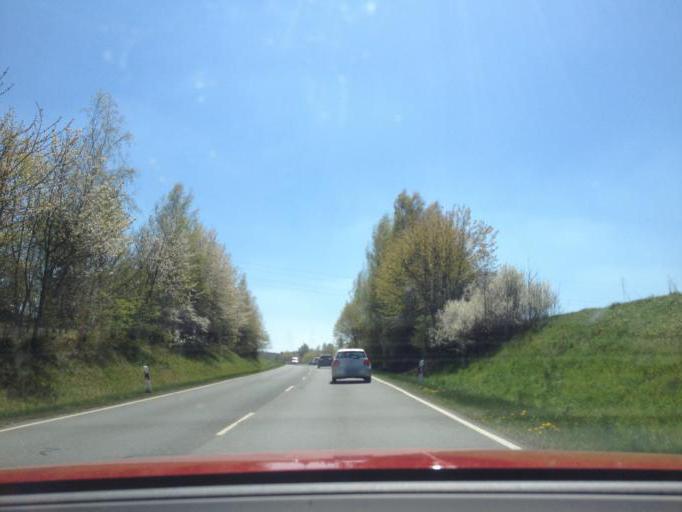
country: DE
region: Bavaria
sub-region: Upper Franconia
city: Schwarzenbach an der Saale
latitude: 50.2367
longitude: 11.9347
